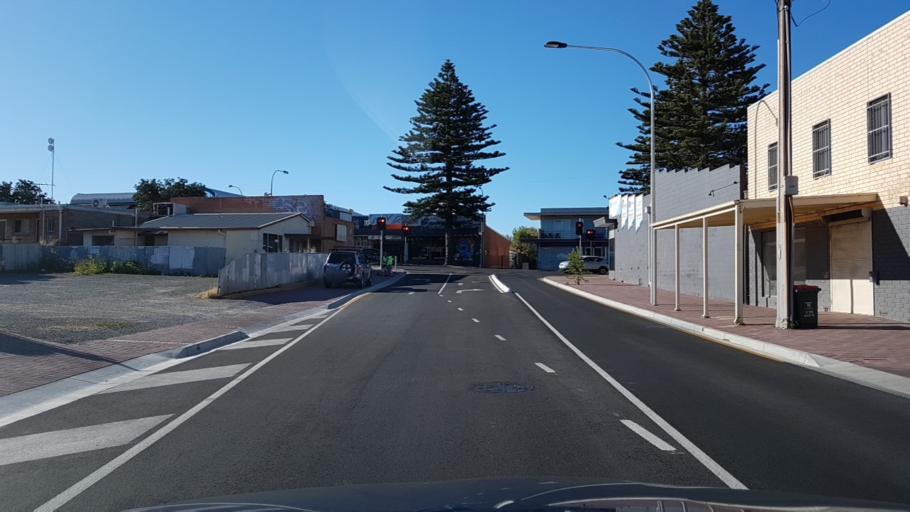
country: AU
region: South Australia
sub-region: Adelaide
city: Port Noarlunga
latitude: -35.1387
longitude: 138.4740
